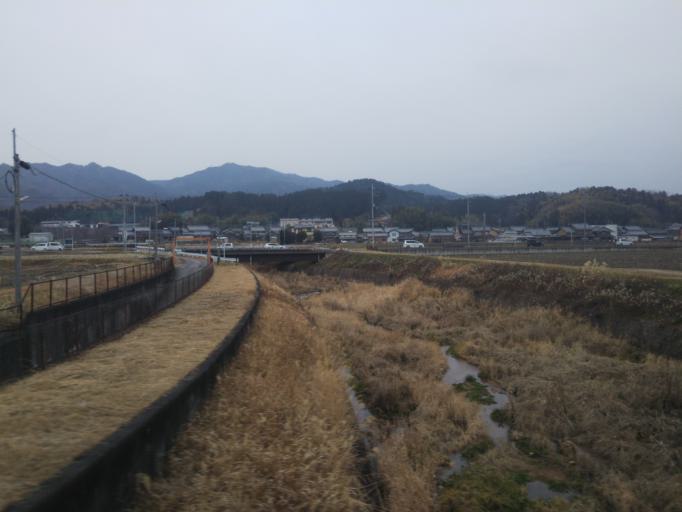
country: JP
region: Shiga Prefecture
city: Minakuchicho-matoba
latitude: 35.0034
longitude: 136.0776
